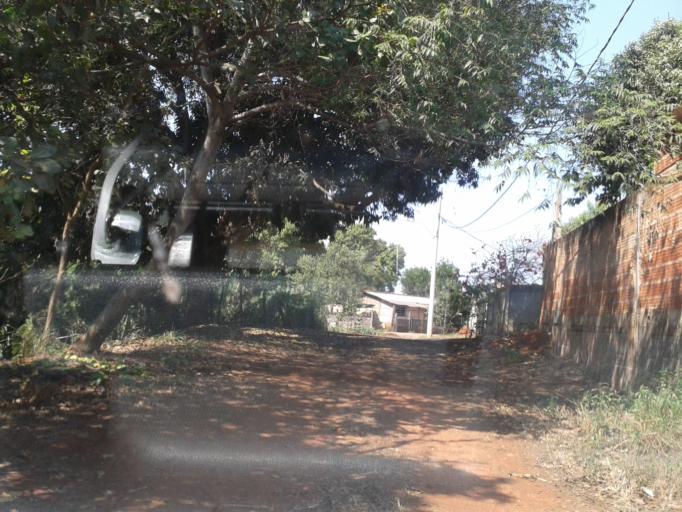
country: BR
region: Minas Gerais
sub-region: Ituiutaba
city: Ituiutaba
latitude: -18.9671
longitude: -49.4824
